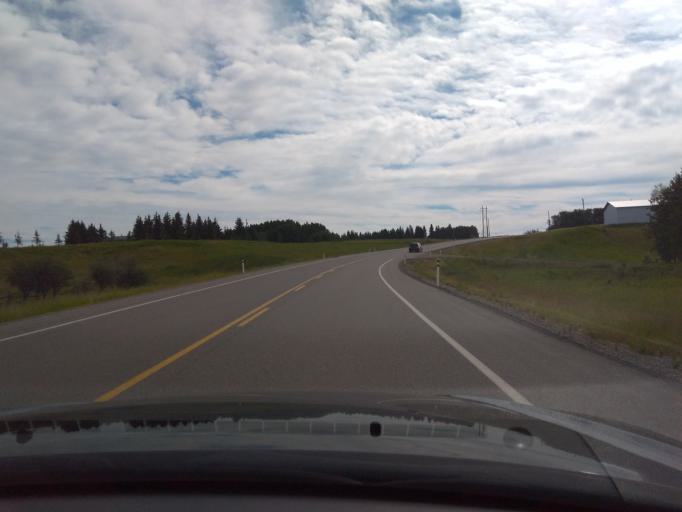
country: CA
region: Alberta
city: Cochrane
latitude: 51.4750
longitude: -114.4340
